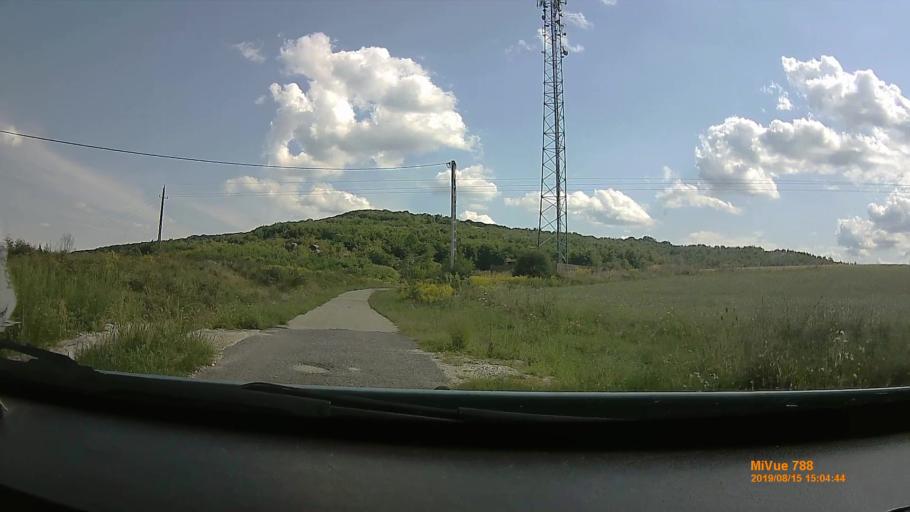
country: HU
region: Borsod-Abauj-Zemplen
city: Sajokaza
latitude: 48.2693
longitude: 20.5558
